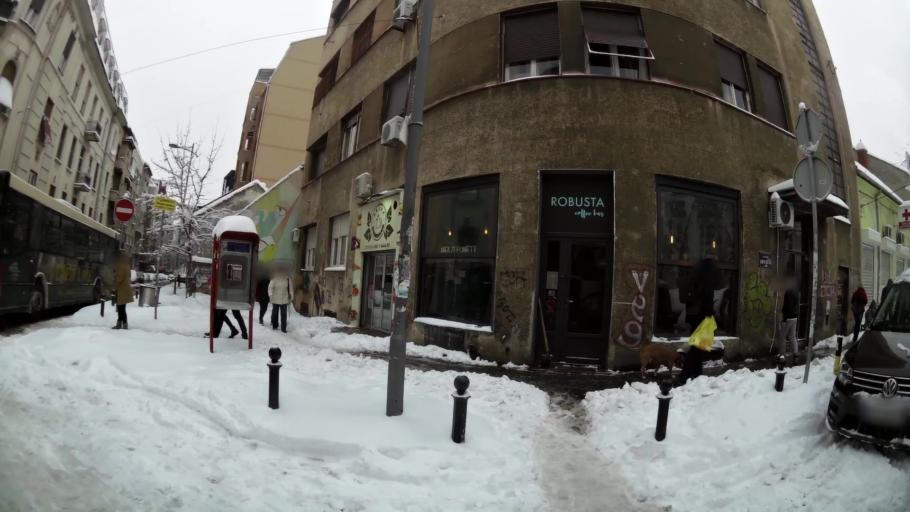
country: RS
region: Central Serbia
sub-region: Belgrade
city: Vracar
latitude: 44.8022
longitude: 20.4755
